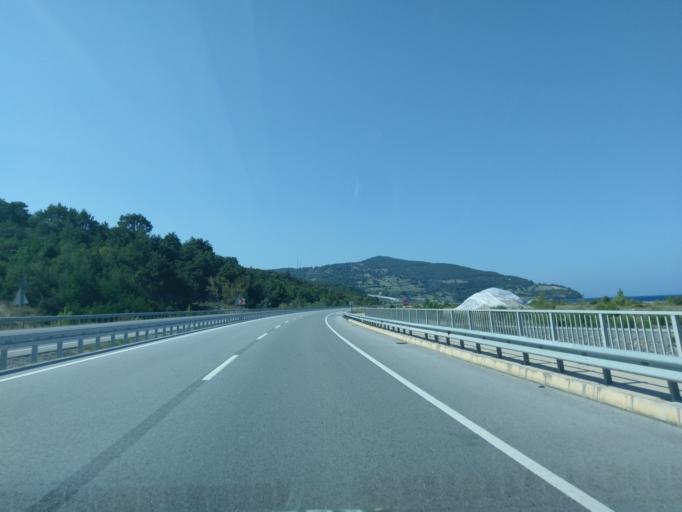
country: TR
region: Sinop
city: Dikmen
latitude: 41.7160
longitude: 35.2761
